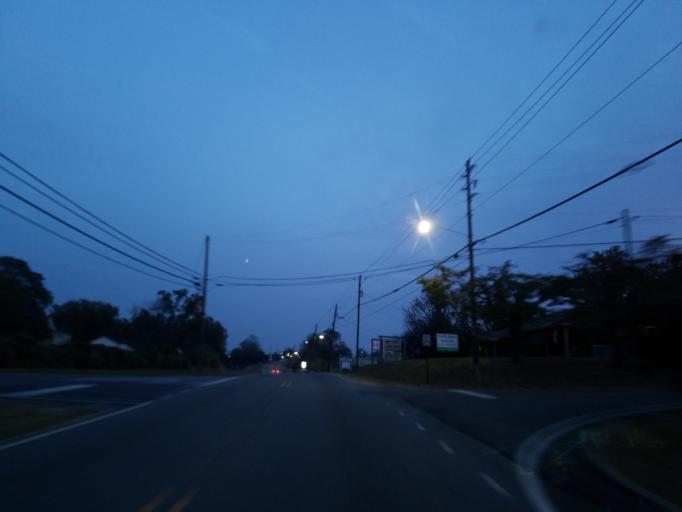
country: US
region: Georgia
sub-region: Pickens County
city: Jasper
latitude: 34.4716
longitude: -84.4350
